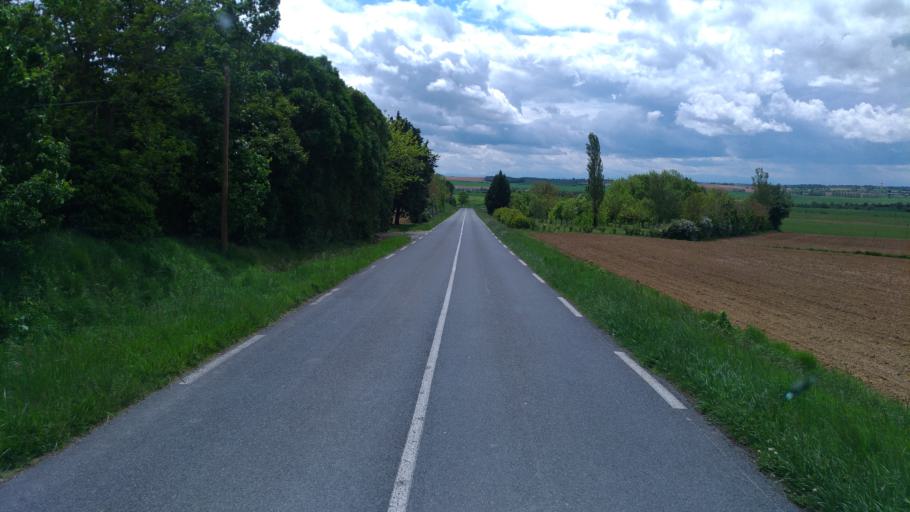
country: FR
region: Midi-Pyrenees
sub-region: Departement de la Haute-Garonne
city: Auriac-sur-Vendinelle
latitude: 43.4579
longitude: 1.8187
